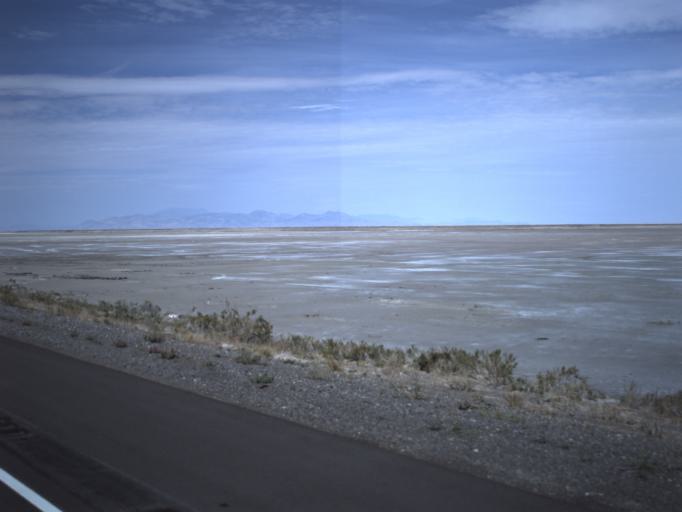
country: US
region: Utah
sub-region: Tooele County
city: Wendover
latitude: 40.7284
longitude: -113.3280
